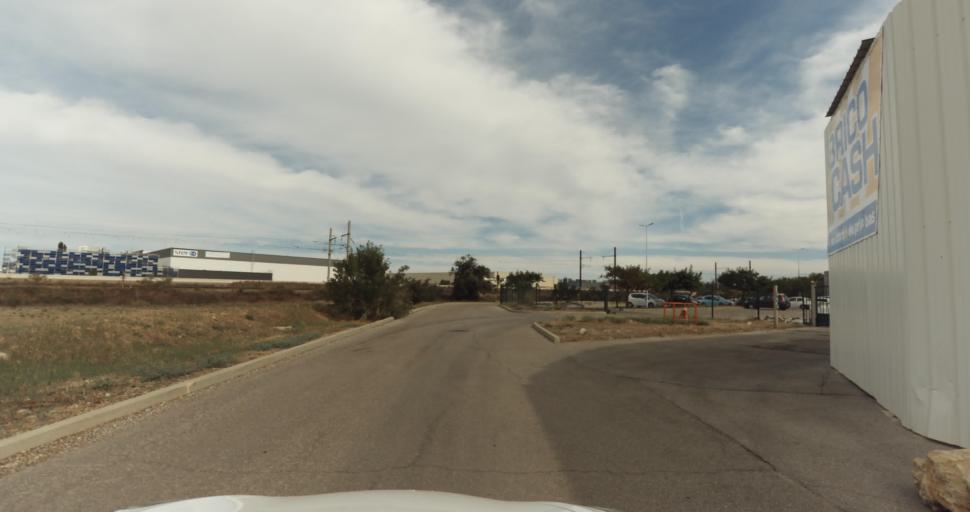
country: FR
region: Provence-Alpes-Cote d'Azur
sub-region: Departement des Bouches-du-Rhone
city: Miramas
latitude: 43.6014
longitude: 5.0022
